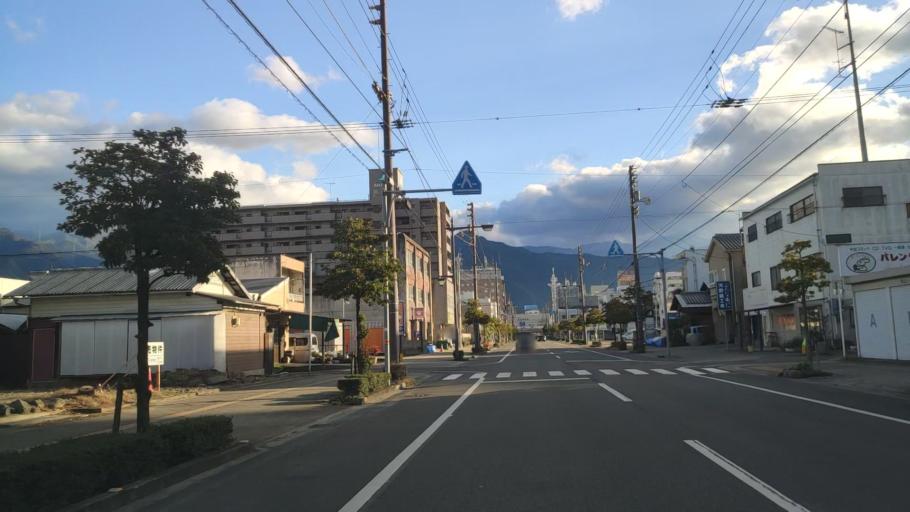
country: JP
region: Ehime
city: Saijo
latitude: 33.9158
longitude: 133.1864
